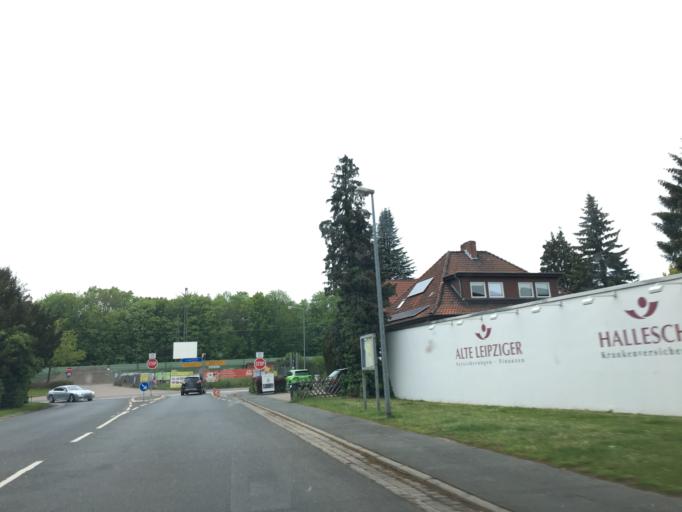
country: DE
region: Lower Saxony
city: Haste
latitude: 52.3811
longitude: 9.3934
